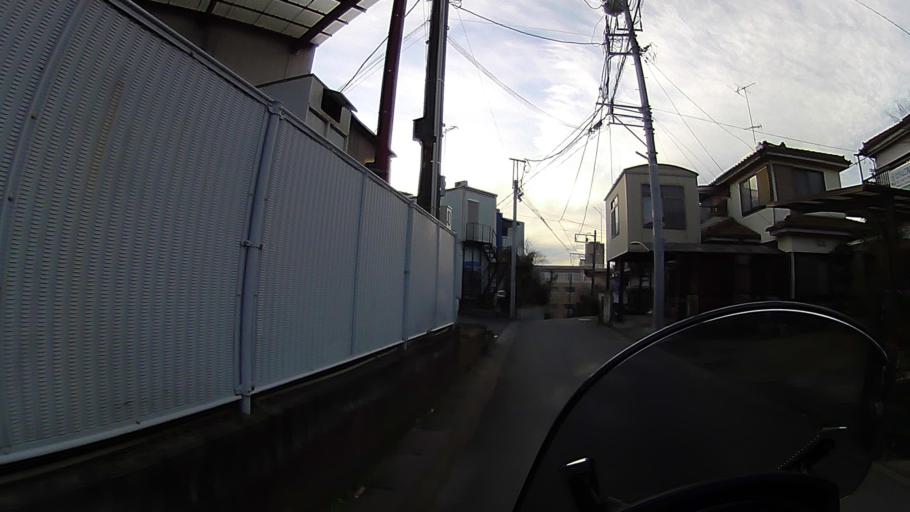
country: JP
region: Kanagawa
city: Atsugi
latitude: 35.4284
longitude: 139.4187
